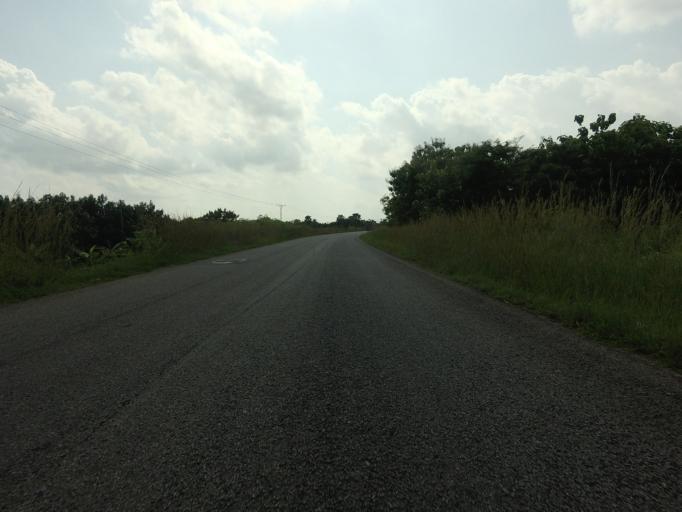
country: GH
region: Volta
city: Ho
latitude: 6.5824
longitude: 0.5757
